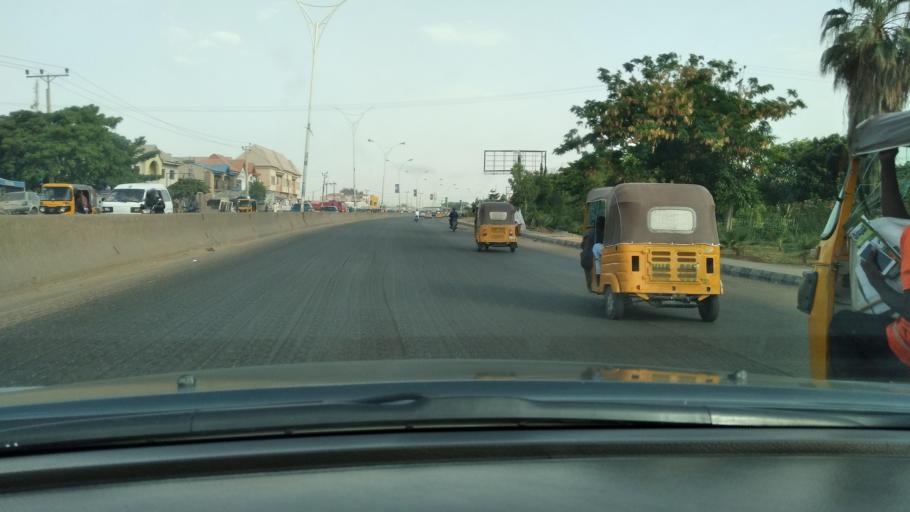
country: NG
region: Kano
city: Kano
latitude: 11.9532
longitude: 8.5639
